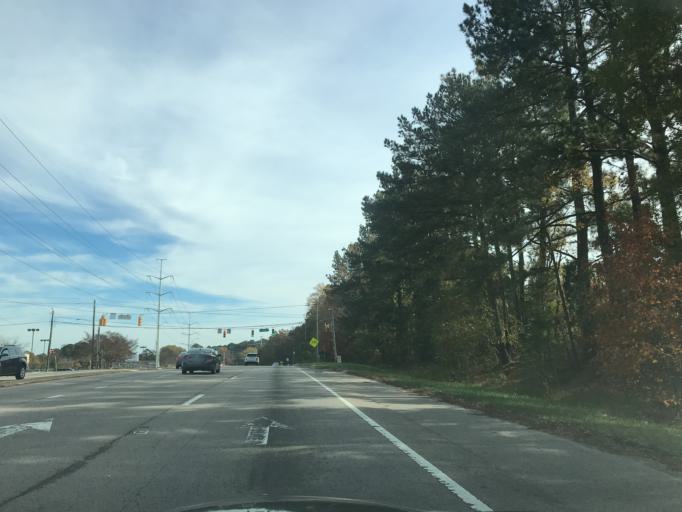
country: US
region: North Carolina
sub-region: Wake County
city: West Raleigh
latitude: 35.8021
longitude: -78.6888
